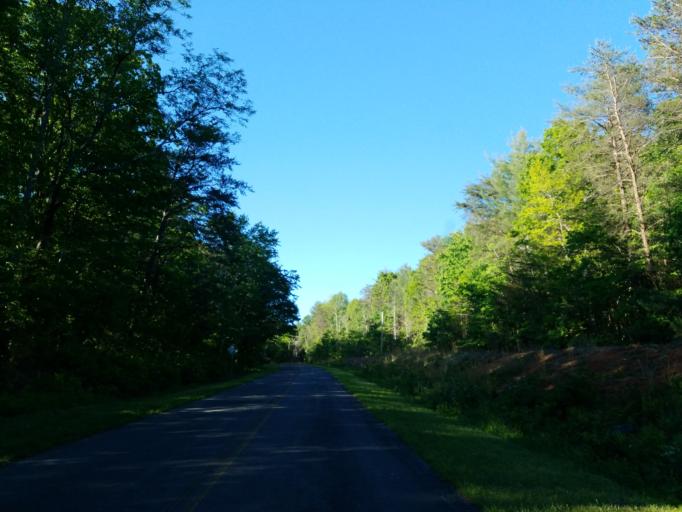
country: US
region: Georgia
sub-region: Fannin County
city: Blue Ridge
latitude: 34.7125
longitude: -84.2914
